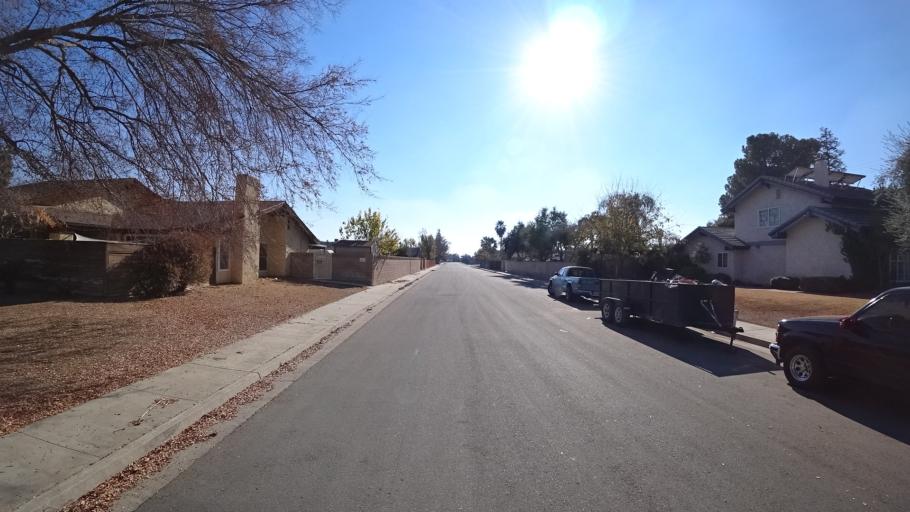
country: US
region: California
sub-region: Kern County
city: Greenfield
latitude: 35.3059
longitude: -119.0453
